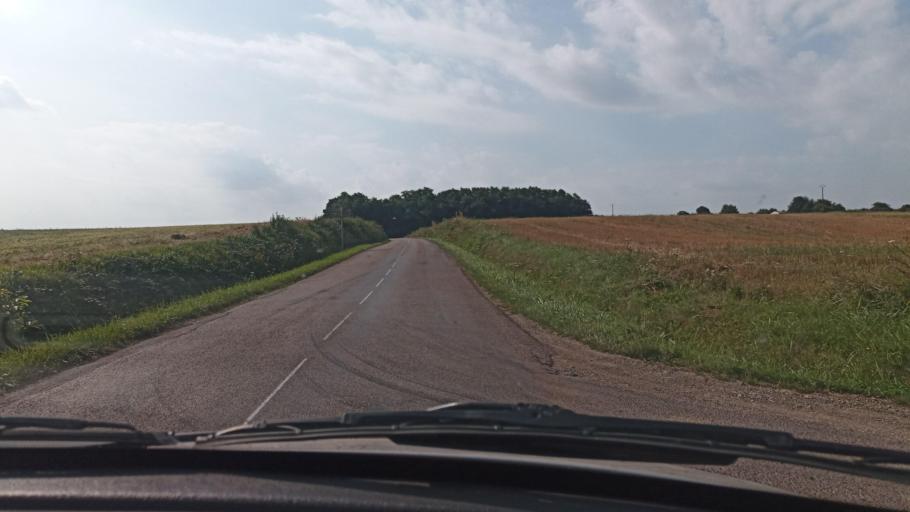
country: FR
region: Bourgogne
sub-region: Departement de l'Yonne
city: Saint-Valerien
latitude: 48.2096
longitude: 3.0737
